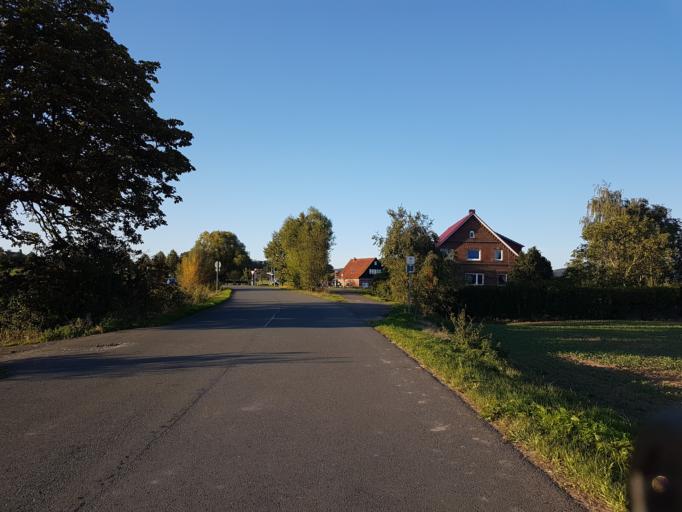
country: DE
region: North Rhine-Westphalia
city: Porta Westfalica
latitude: 52.1947
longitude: 8.9799
